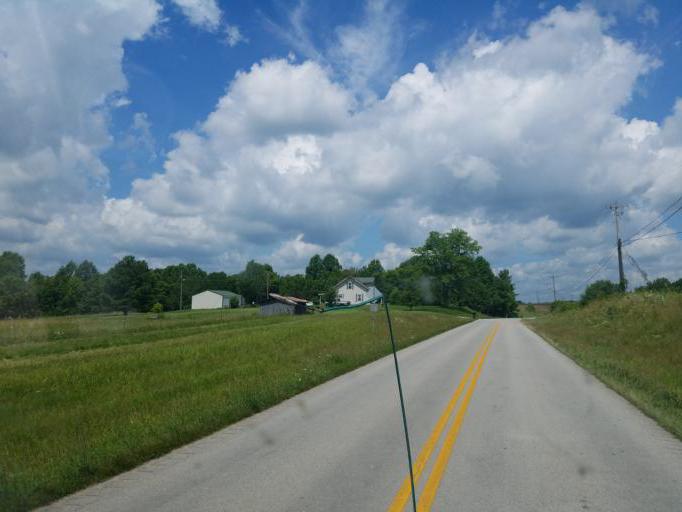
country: US
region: Kentucky
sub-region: Grayson County
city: Leitchfield
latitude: 37.5084
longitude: -86.3234
